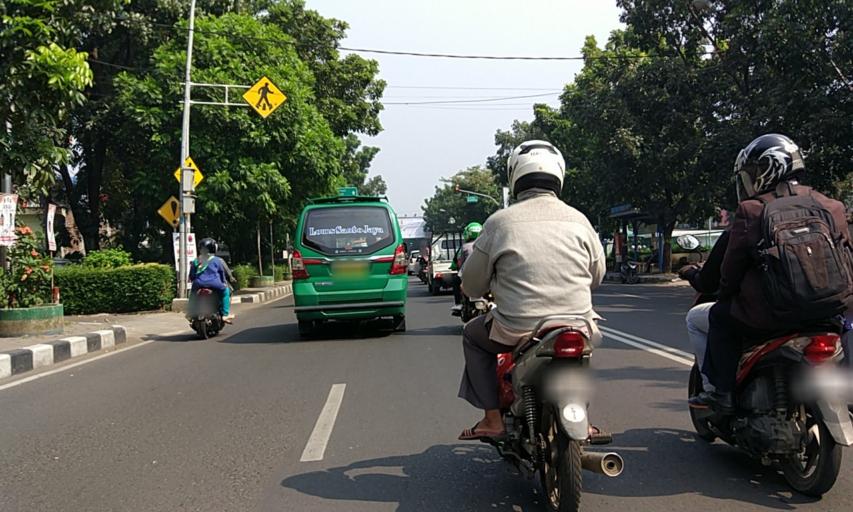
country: ID
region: West Java
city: Bandung
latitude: -6.8988
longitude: 107.6382
